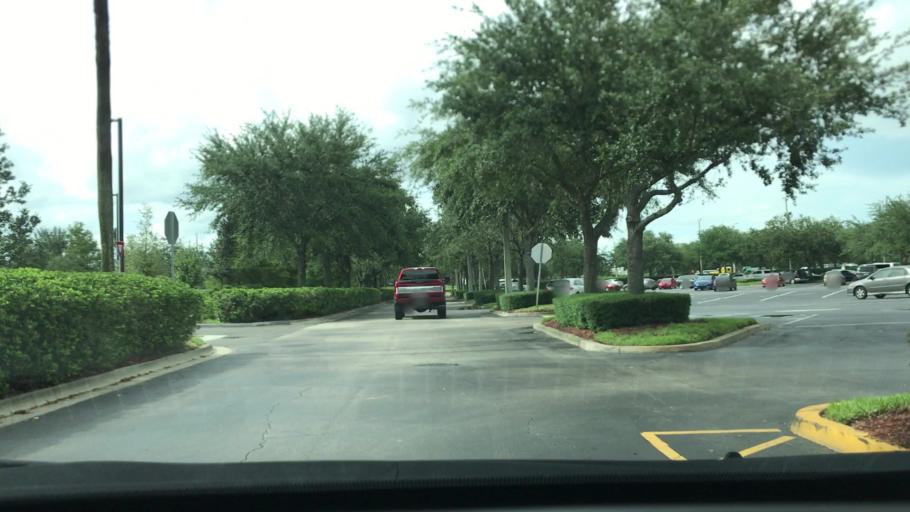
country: US
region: Florida
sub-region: Orange County
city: Williamsburg
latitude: 28.3861
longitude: -81.4869
